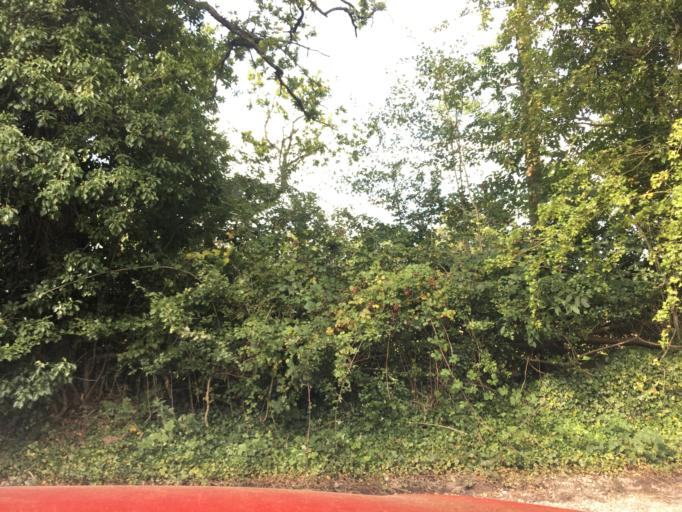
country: GB
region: England
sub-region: South Gloucestershire
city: Falfield
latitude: 51.6045
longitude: -2.4442
